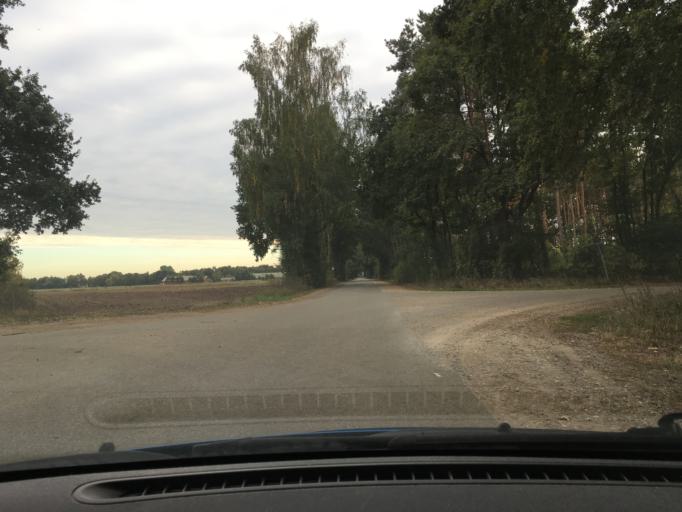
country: DE
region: Lower Saxony
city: Winsen
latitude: 53.3635
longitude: 10.2354
